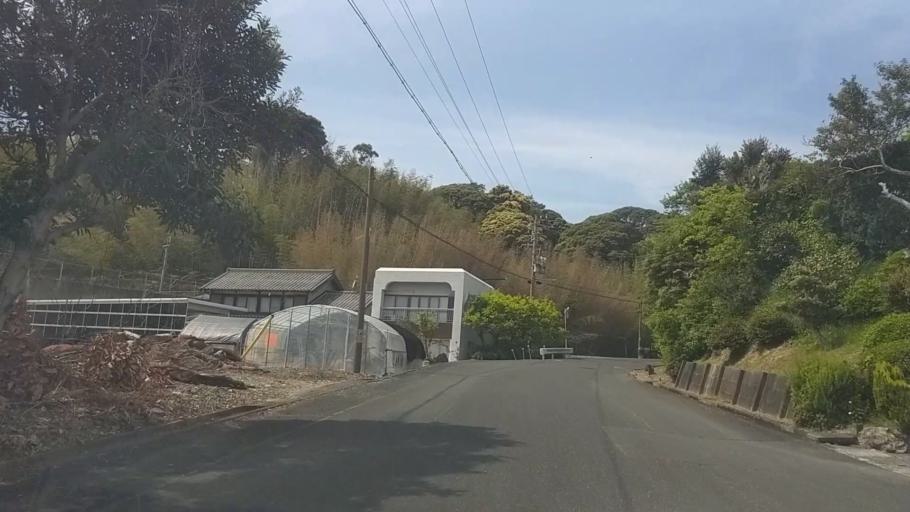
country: JP
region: Shizuoka
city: Kosai-shi
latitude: 34.7700
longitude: 137.6279
